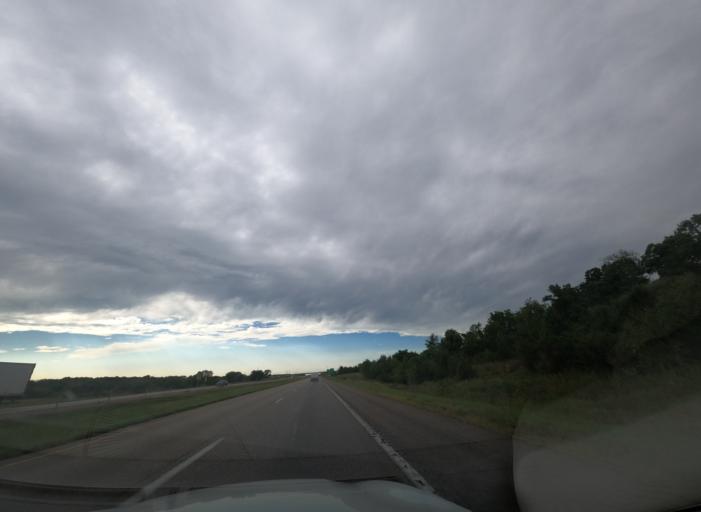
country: US
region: Missouri
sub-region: Sainte Genevieve County
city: Sainte Genevieve
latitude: 37.9310
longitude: -90.1148
